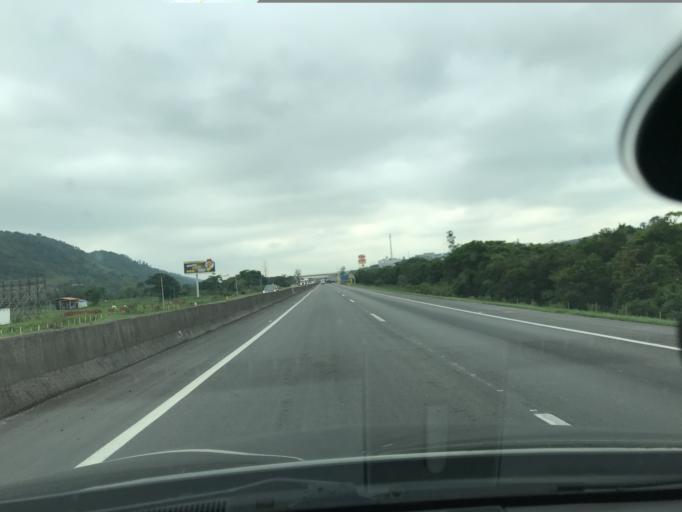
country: BR
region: Sao Paulo
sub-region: Santa Isabel
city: Santa Isabel
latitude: -23.3442
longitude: -46.1606
